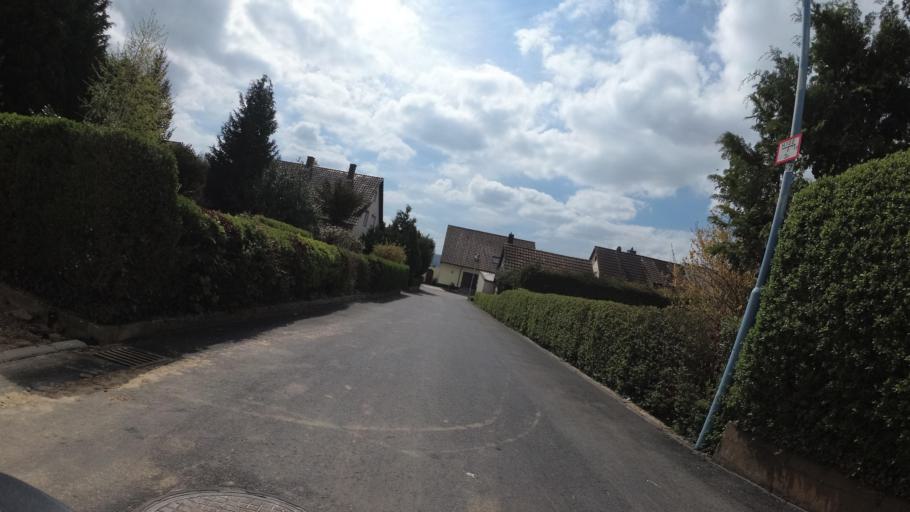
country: DE
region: Baden-Wuerttemberg
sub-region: Regierungsbezirk Stuttgart
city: Neuenstadt am Kocher
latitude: 49.2454
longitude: 9.3353
